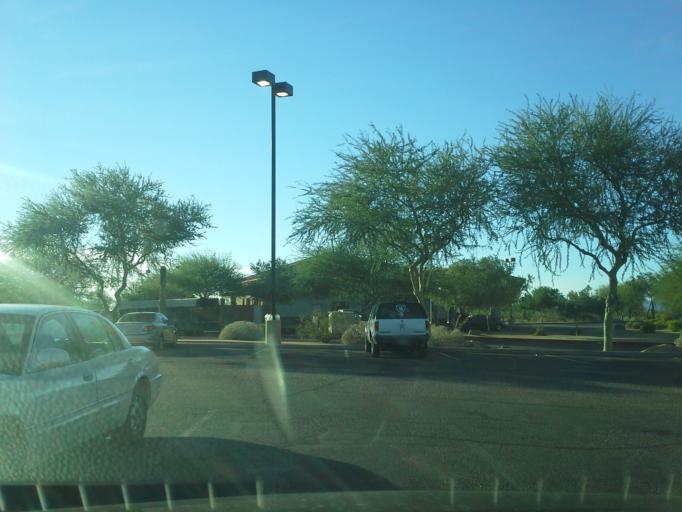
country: US
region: Arizona
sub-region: Pinal County
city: Apache Junction
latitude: 33.3666
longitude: -111.4757
